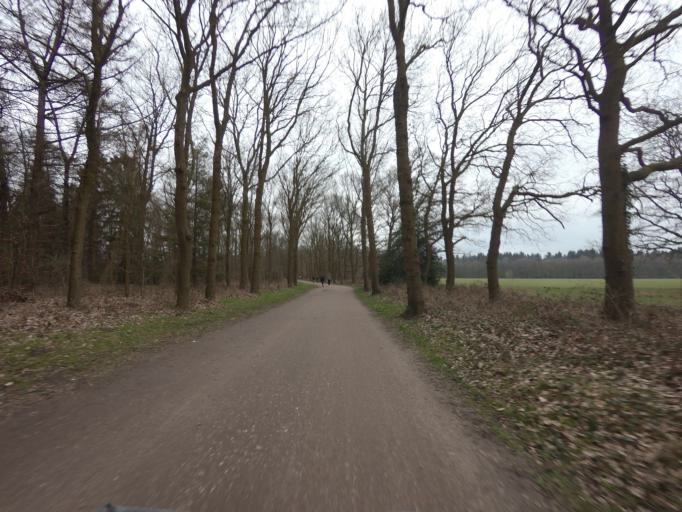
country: NL
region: North Holland
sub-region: Gemeente Hilversum
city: Hilversum
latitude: 52.2300
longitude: 5.1488
